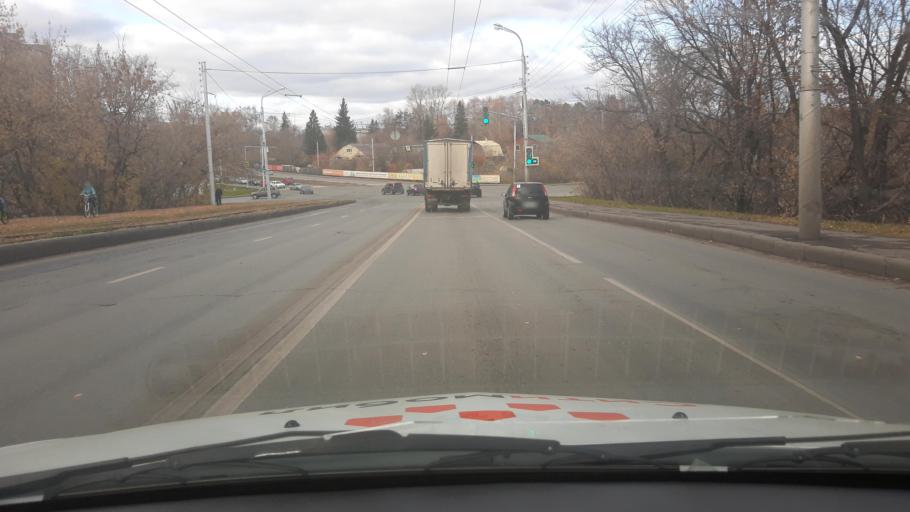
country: RU
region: Bashkortostan
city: Ufa
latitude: 54.8019
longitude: 56.1378
